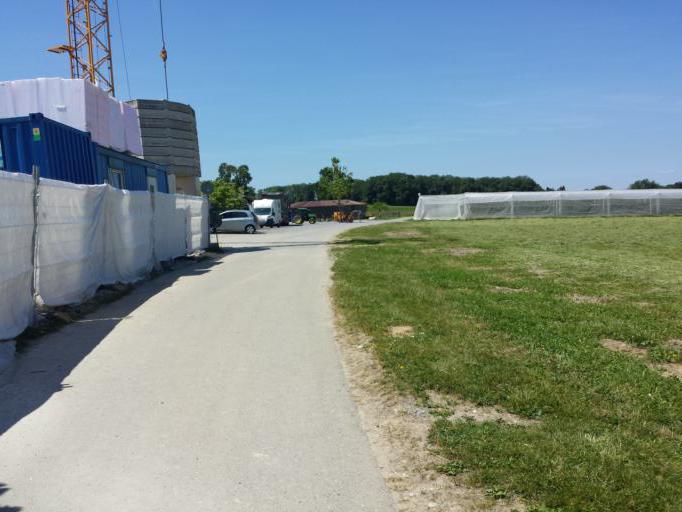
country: CH
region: Thurgau
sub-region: Arbon District
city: Romanshorn
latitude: 47.5755
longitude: 9.3630
